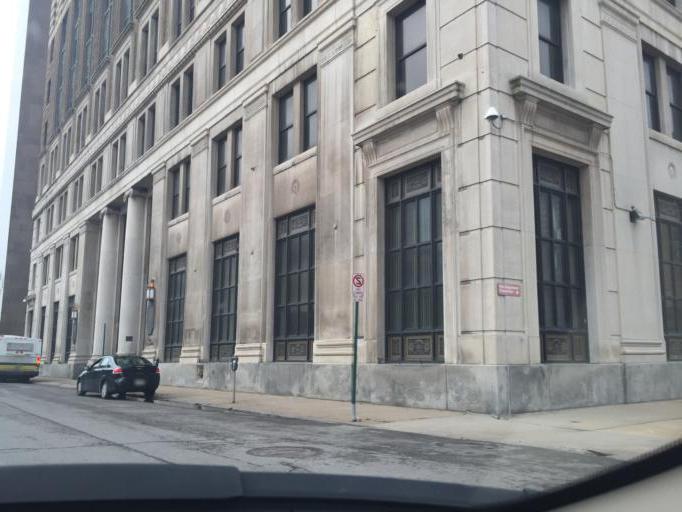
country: US
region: Michigan
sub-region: Wayne County
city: Detroit
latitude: 42.3330
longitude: -83.0535
